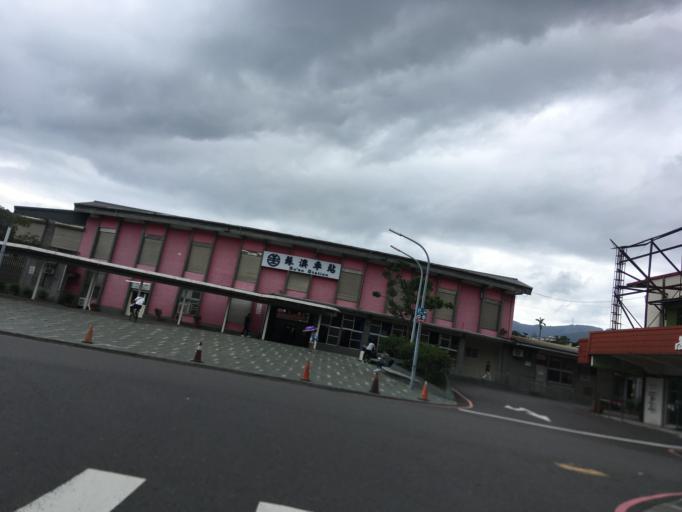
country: TW
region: Taiwan
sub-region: Yilan
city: Yilan
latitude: 24.5956
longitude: 121.8514
